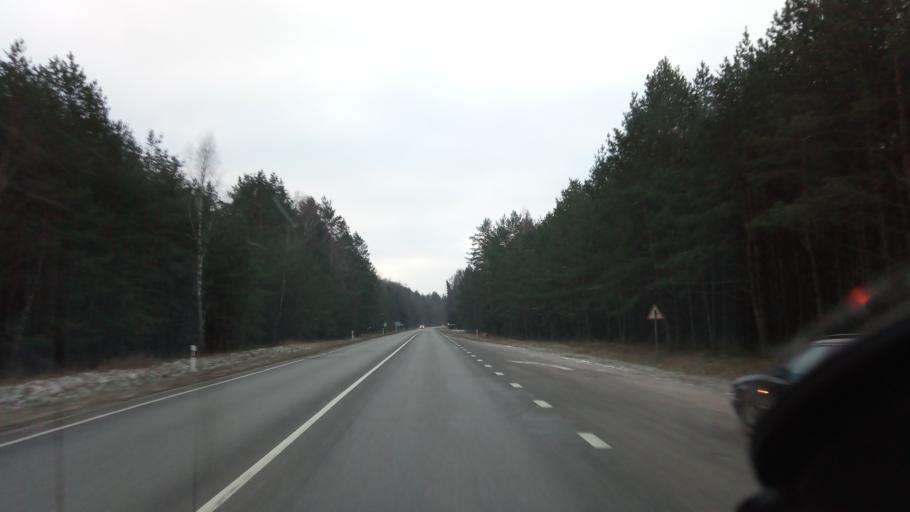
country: LT
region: Vilnius County
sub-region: Trakai
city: Rudiskes
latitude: 54.4248
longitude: 24.9794
